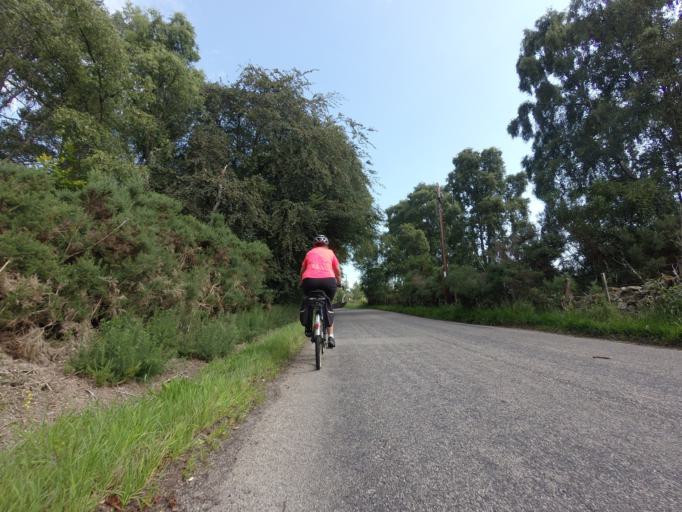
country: GB
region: Scotland
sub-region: Highland
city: Invergordon
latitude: 57.7312
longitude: -4.1920
